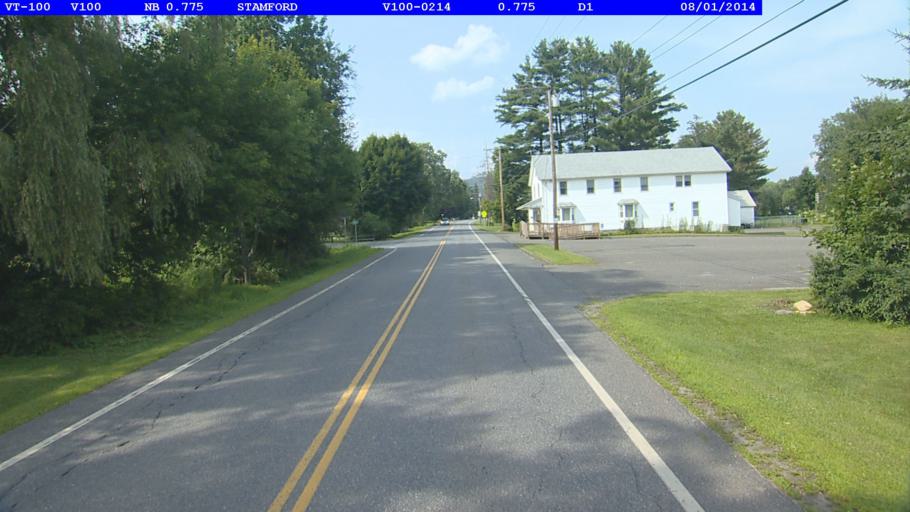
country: US
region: Massachusetts
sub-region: Berkshire County
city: North Adams
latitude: 42.7518
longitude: -73.0686
